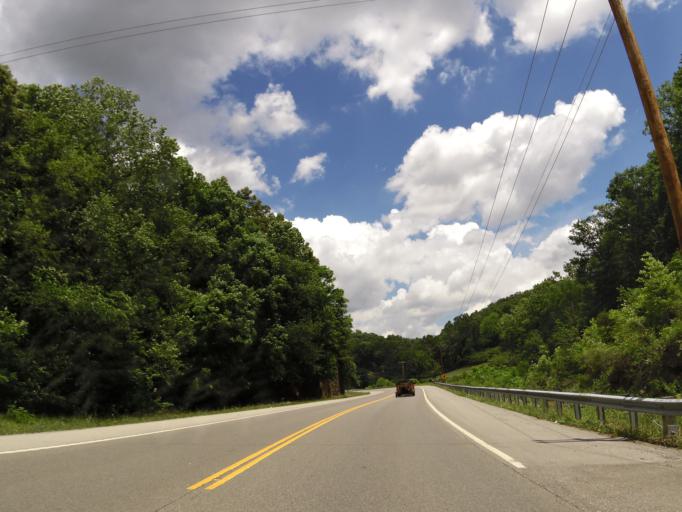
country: US
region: Tennessee
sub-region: Claiborne County
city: New Tazewell
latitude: 36.3873
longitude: -83.7088
